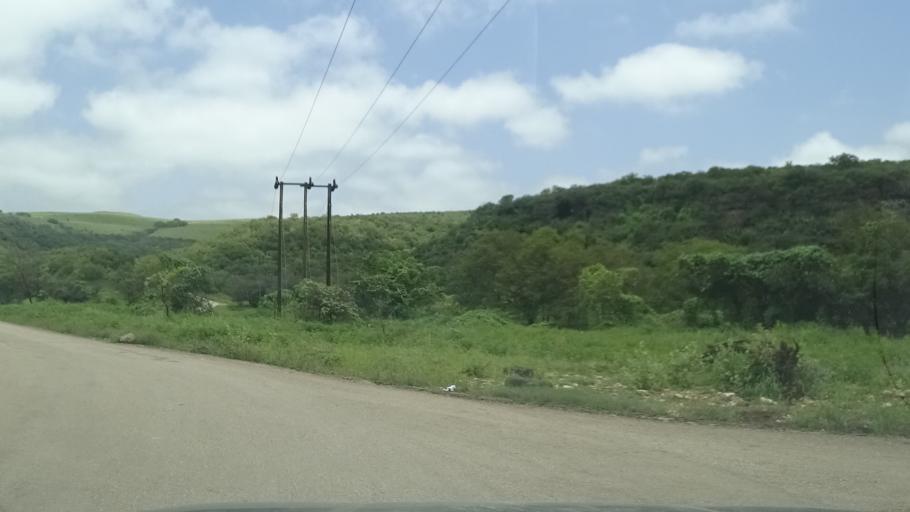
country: OM
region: Zufar
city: Salalah
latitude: 17.1972
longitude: 54.1818
